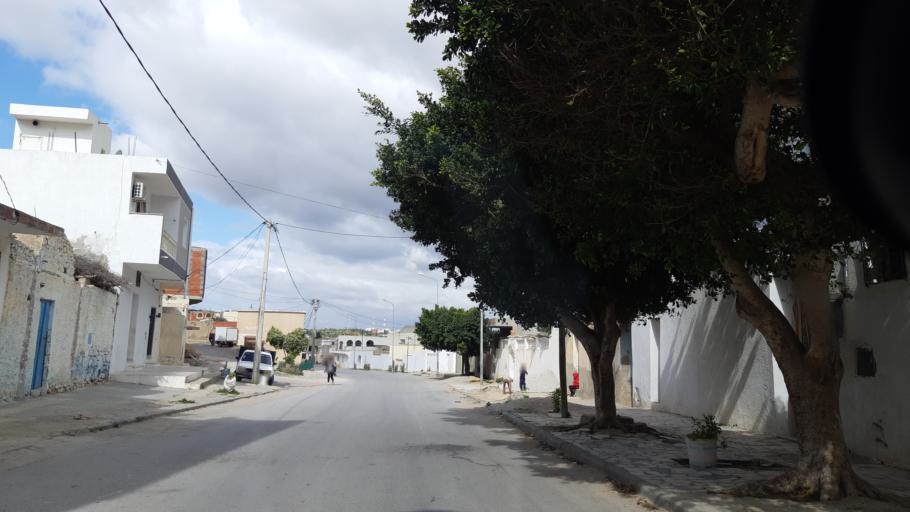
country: TN
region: Susah
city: Akouda
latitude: 35.8717
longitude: 10.5253
